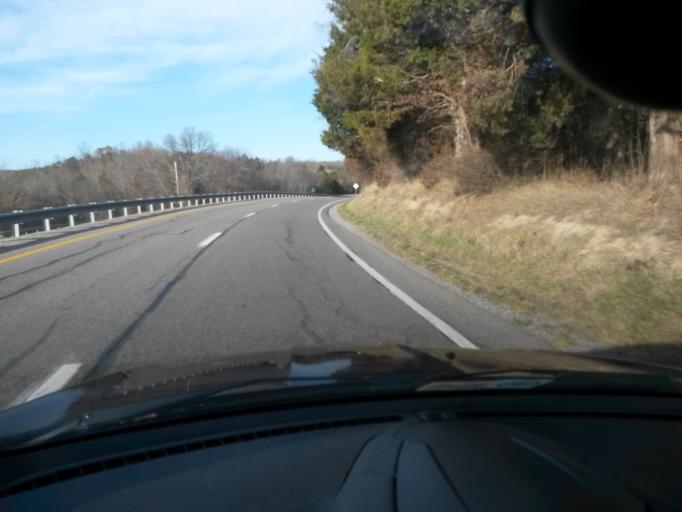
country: US
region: Virginia
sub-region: Botetourt County
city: Fincastle
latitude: 37.5212
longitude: -79.8779
